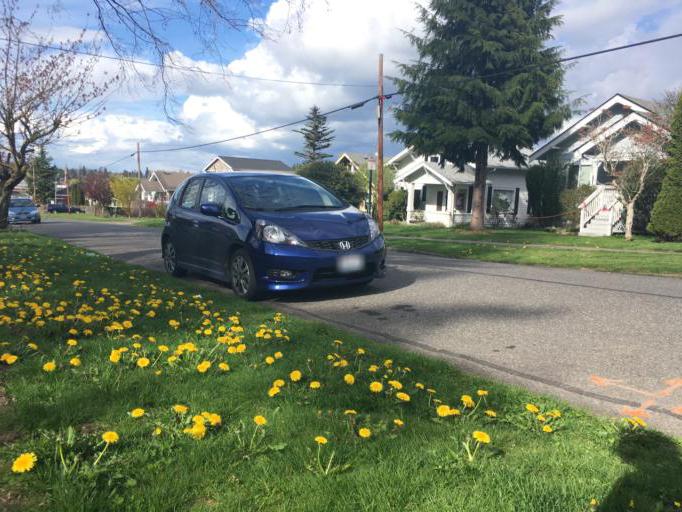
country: US
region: Washington
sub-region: Whatcom County
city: Bellingham
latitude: 48.7520
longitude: -122.4651
